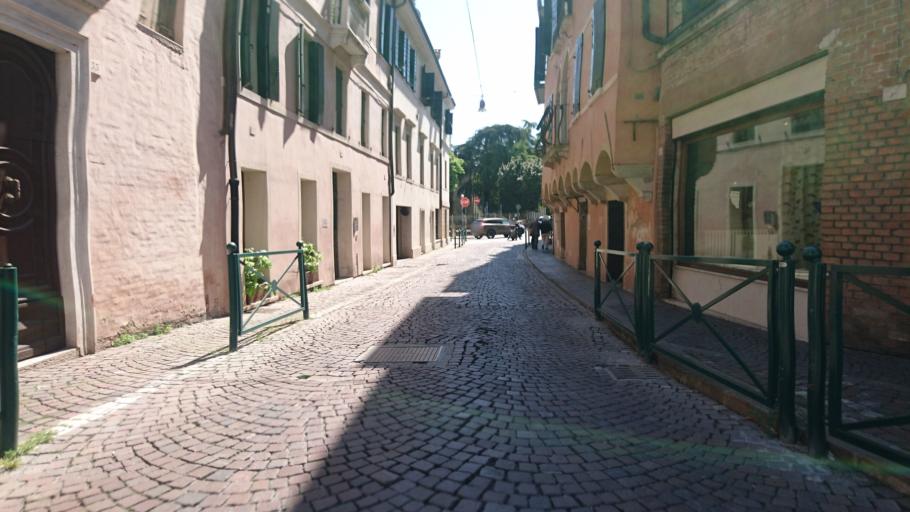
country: IT
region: Veneto
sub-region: Provincia di Treviso
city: Treviso
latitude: 45.6641
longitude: 12.2483
